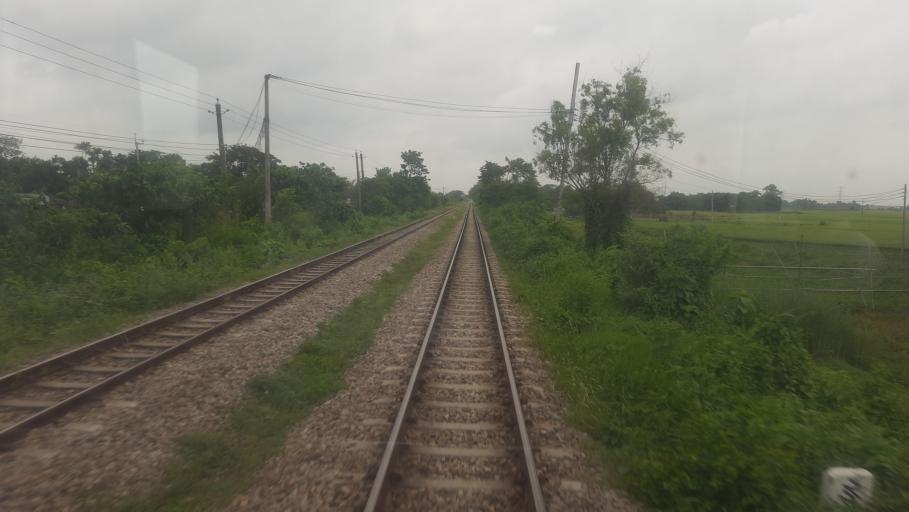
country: BD
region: Dhaka
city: Bhairab Bazar
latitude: 23.9810
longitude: 91.0766
